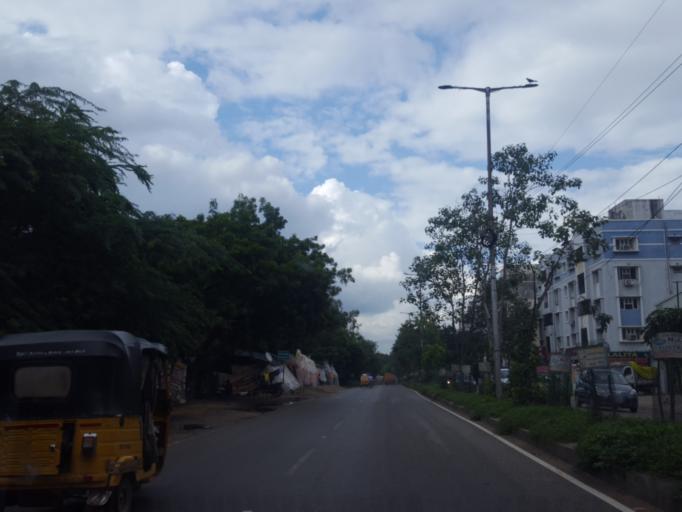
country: IN
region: Telangana
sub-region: Medak
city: Serilingampalle
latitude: 17.4880
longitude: 78.3136
